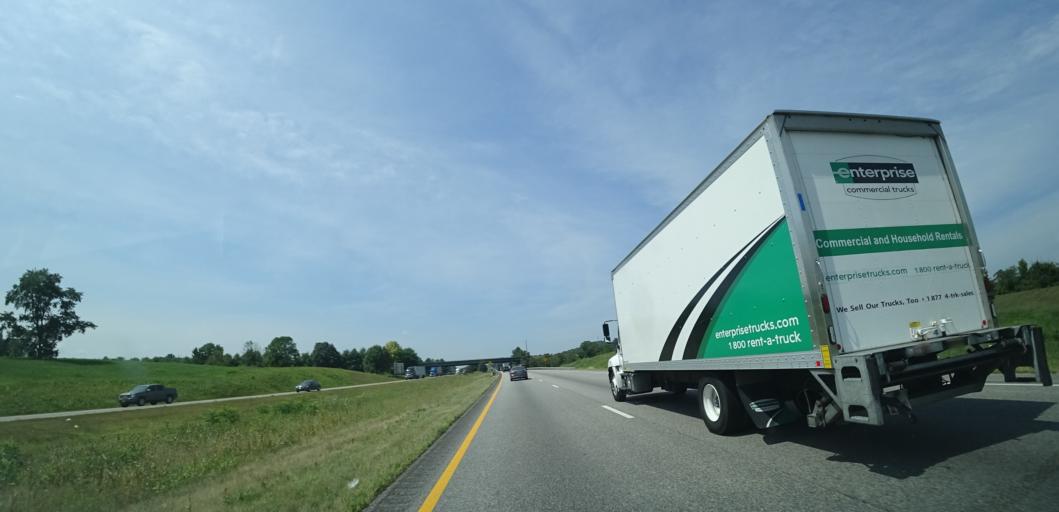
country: US
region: Virginia
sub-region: Augusta County
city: Jolivue
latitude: 38.1232
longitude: -79.0455
